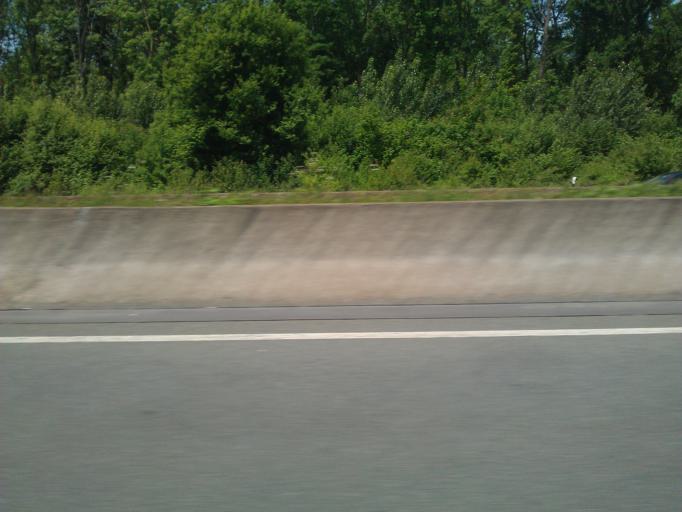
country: DE
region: North Rhine-Westphalia
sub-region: Regierungsbezirk Koln
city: Kerpen
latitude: 50.8966
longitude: 6.6994
